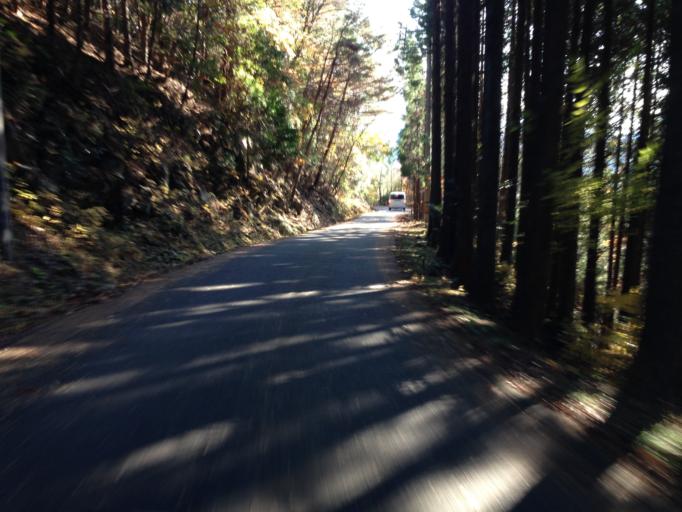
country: JP
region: Gifu
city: Mitake
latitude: 35.6144
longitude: 137.2154
